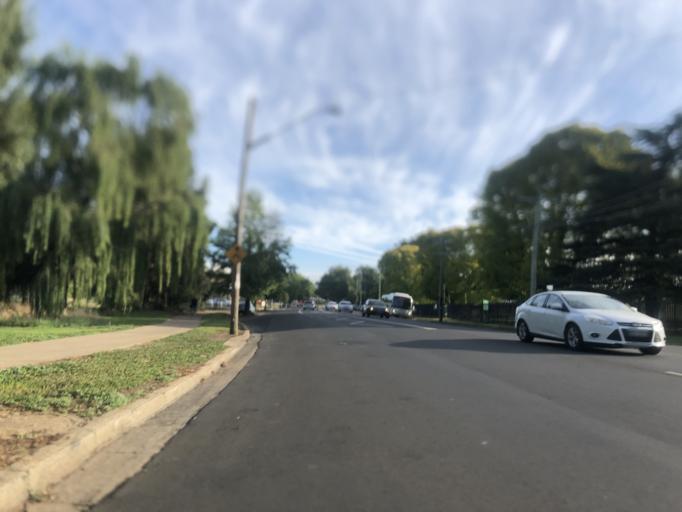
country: AU
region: New South Wales
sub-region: Orange Municipality
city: Orange
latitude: -33.2894
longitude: 149.0975
